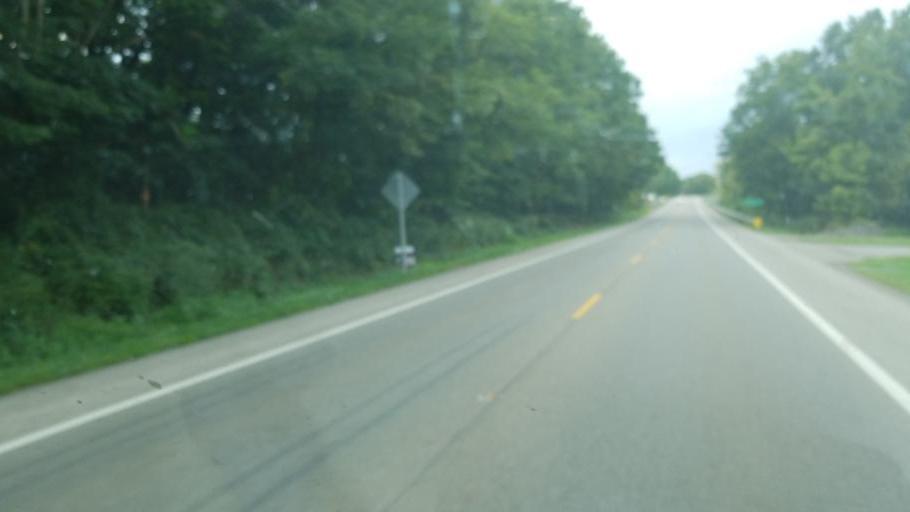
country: US
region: Ohio
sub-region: Tuscarawas County
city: Sugarcreek
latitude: 40.5170
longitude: -81.6674
